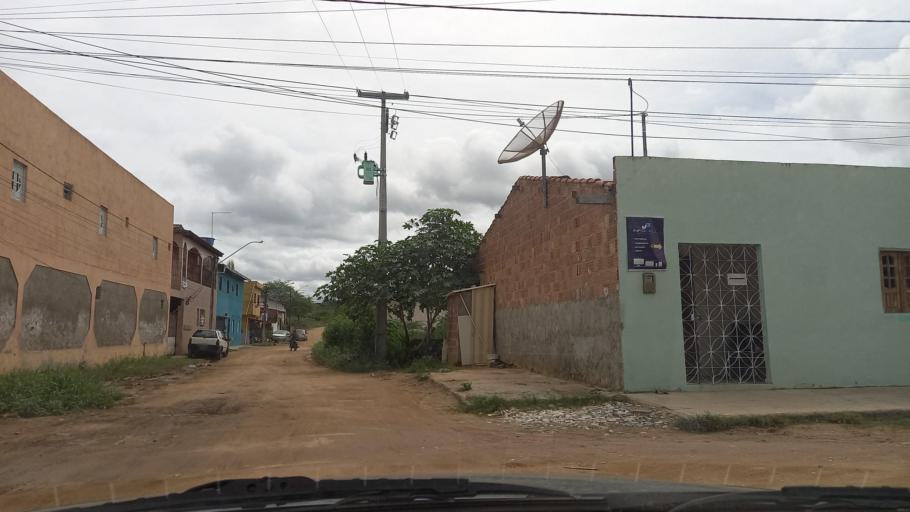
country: BR
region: Pernambuco
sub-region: Gravata
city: Gravata
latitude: -8.1935
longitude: -35.5800
